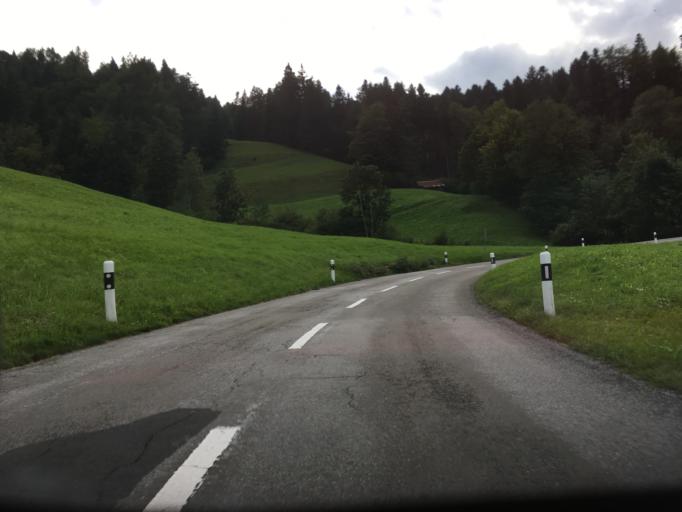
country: CH
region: Thurgau
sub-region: Muenchwilen District
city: Fischingen
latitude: 47.3643
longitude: 8.9739
